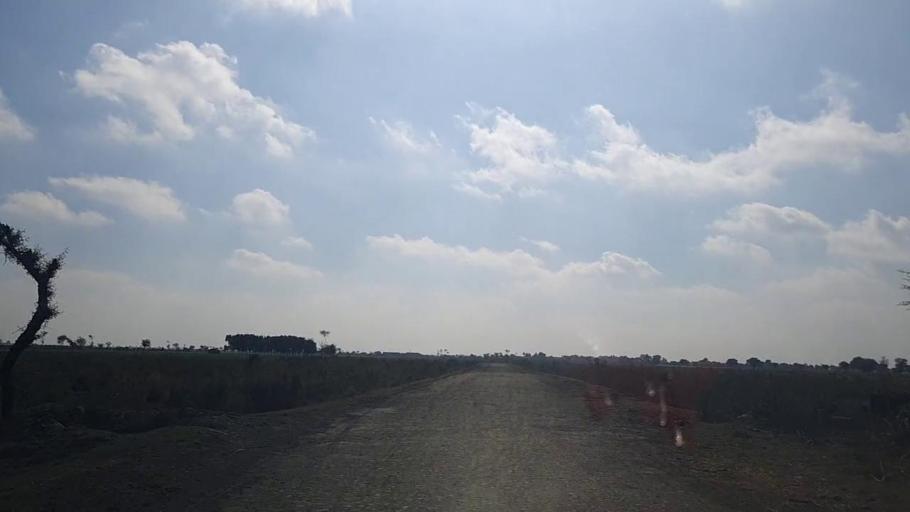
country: PK
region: Sindh
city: Sanghar
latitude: 26.0549
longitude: 69.0055
